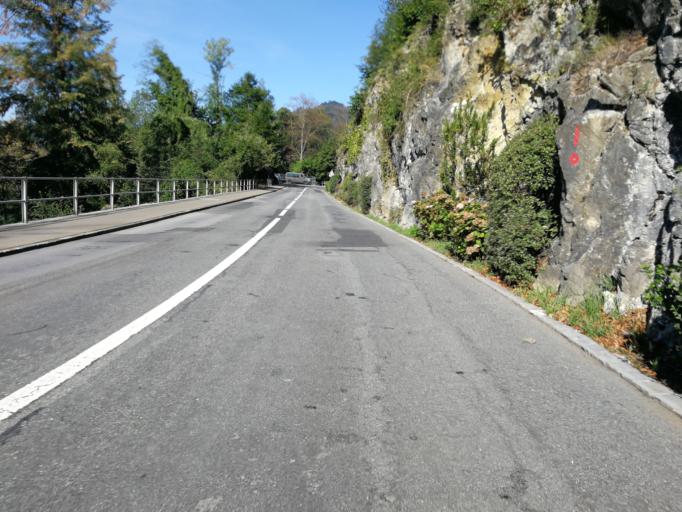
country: CH
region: Lucerne
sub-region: Lucerne-Land District
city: Vitznau
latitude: 46.9951
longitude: 8.4762
